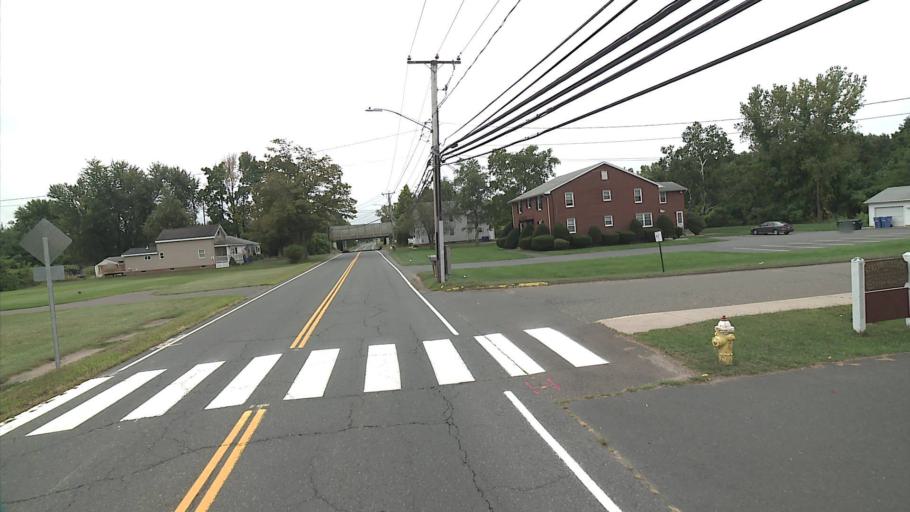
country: US
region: Connecticut
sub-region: Hartford County
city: Windsor Locks
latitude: 41.9204
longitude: -72.6164
